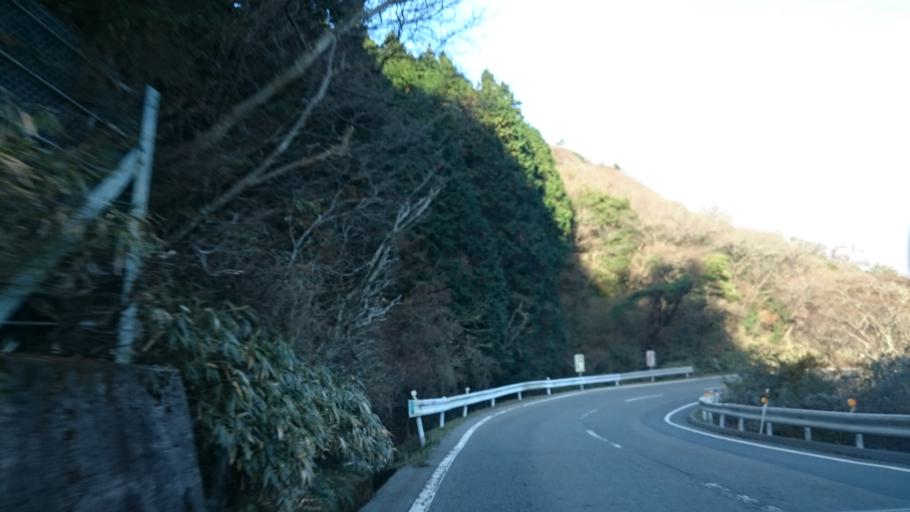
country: JP
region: Shizuoka
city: Heda
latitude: 34.9723
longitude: 138.8411
